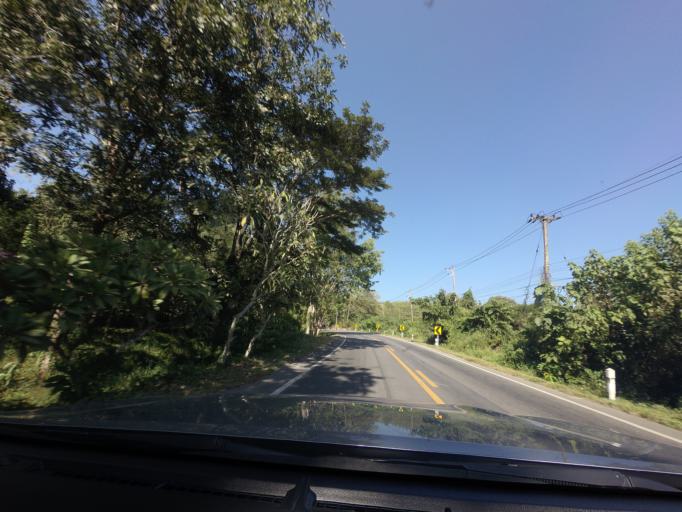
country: TH
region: Sukhothai
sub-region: Amphoe Si Satchanalai
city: Si Satchanalai
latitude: 17.6142
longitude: 99.7088
